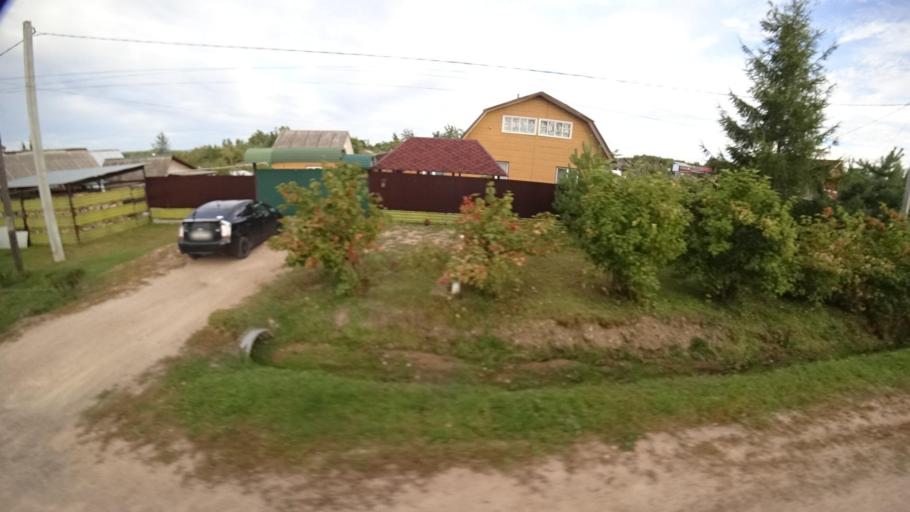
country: RU
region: Primorskiy
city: Yakovlevka
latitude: 44.4167
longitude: 133.4708
